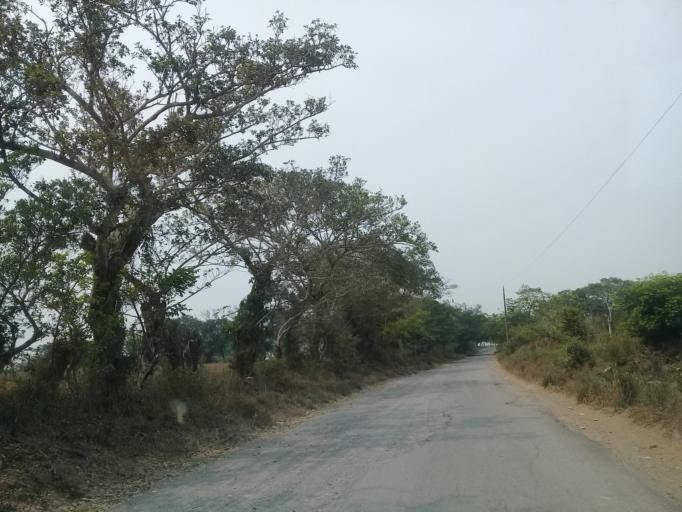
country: MX
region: Veracruz
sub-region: Medellin
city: La Laguna y Monte del Castillo
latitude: 18.9509
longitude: -96.1261
